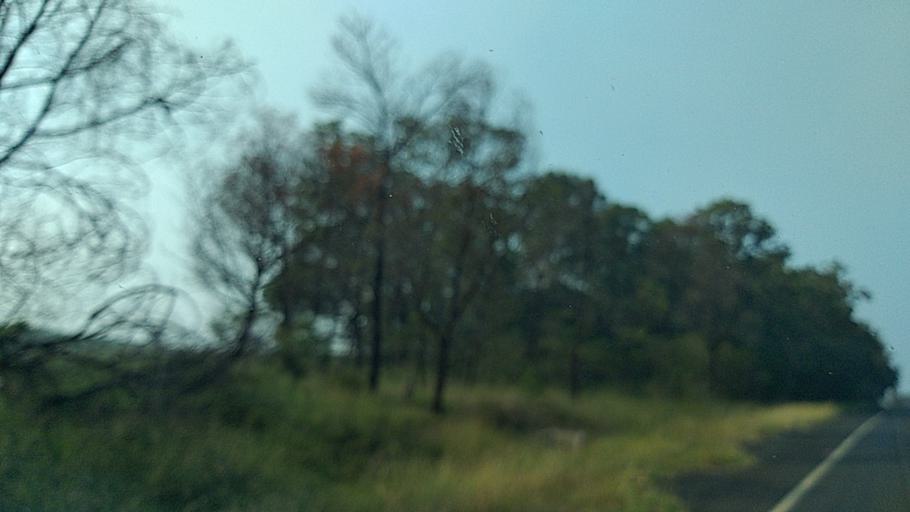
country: AU
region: New South Wales
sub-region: Wollondilly
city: Douglas Park
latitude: -34.2216
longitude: 150.7634
